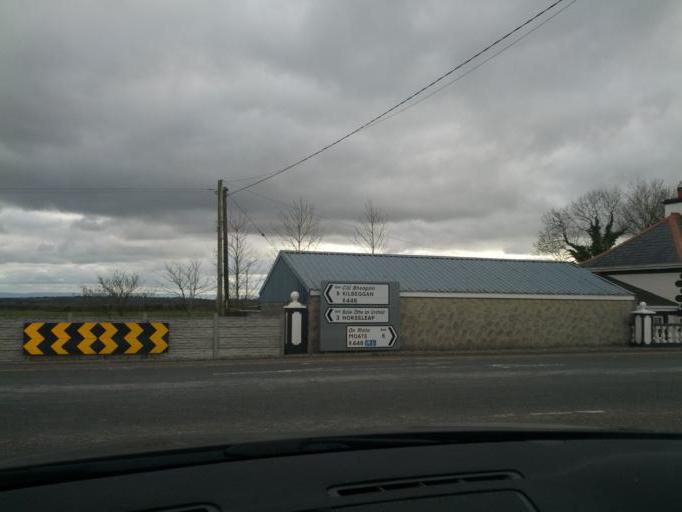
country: IE
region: Leinster
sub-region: Uibh Fhaili
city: Clara
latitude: 53.3989
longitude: -7.6198
